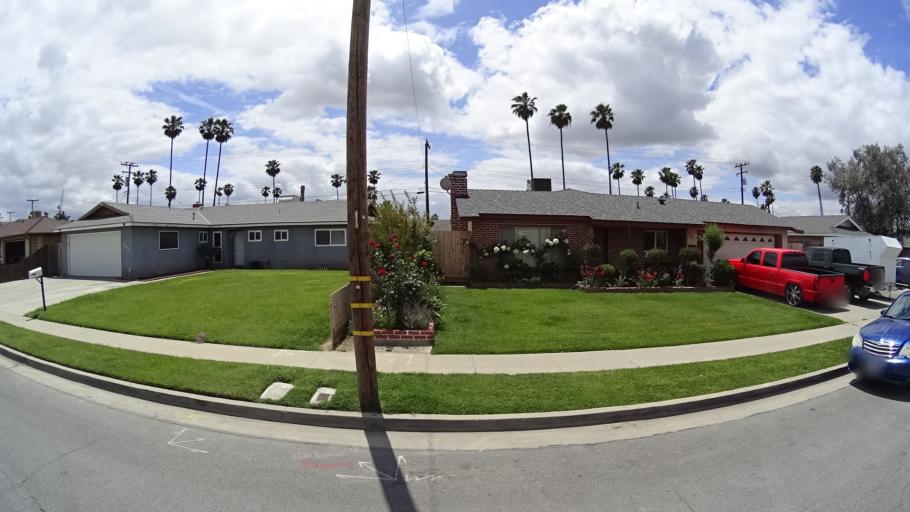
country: US
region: California
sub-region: Kings County
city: Hanford
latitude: 36.3393
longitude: -119.6248
